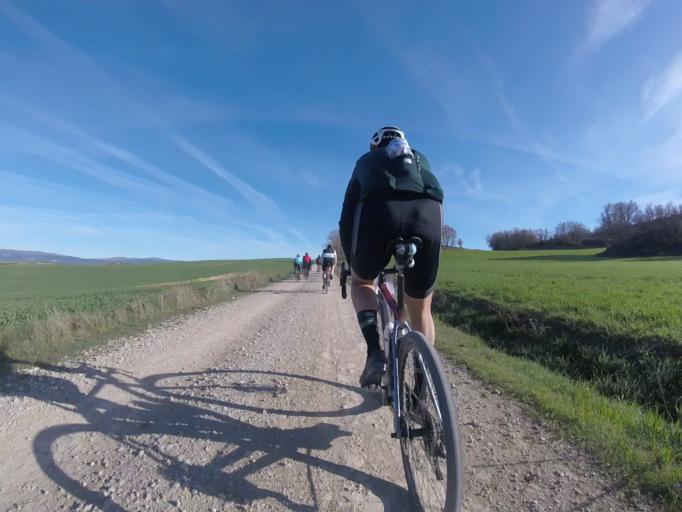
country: ES
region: Navarre
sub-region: Provincia de Navarra
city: Villatuerta
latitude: 42.6555
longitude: -1.9699
